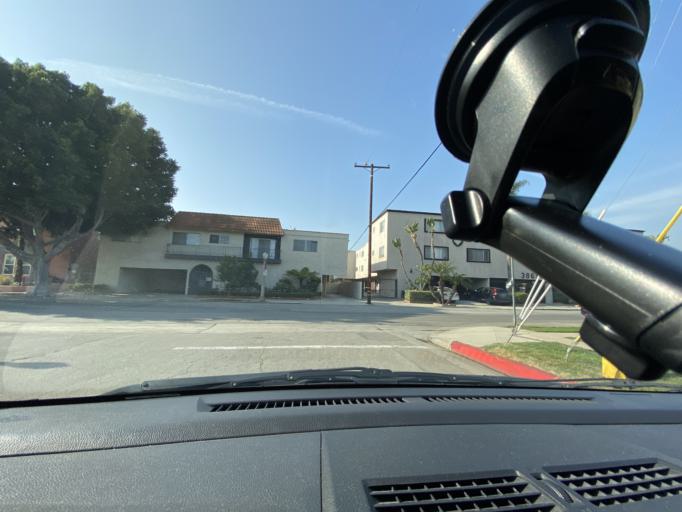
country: US
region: California
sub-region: Los Angeles County
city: Culver City
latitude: 34.0126
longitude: -118.4133
